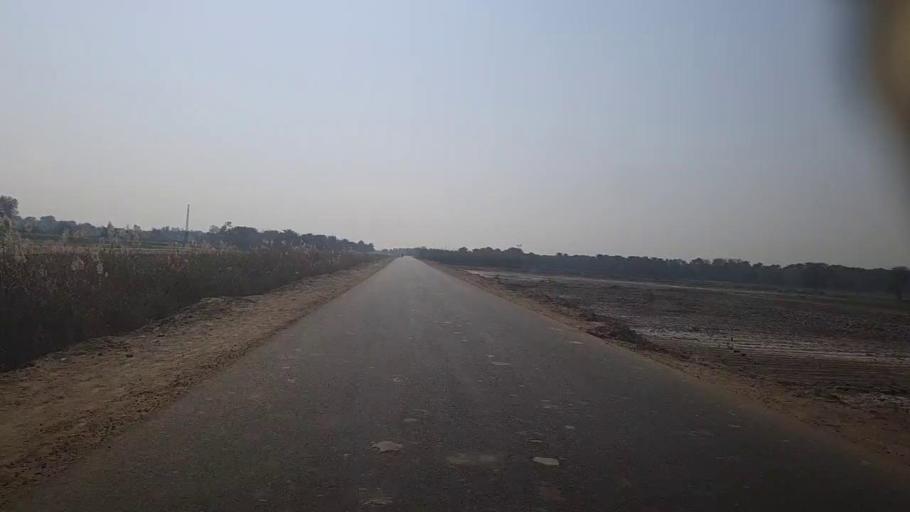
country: PK
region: Sindh
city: Khairpur
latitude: 27.4708
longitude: 68.8211
